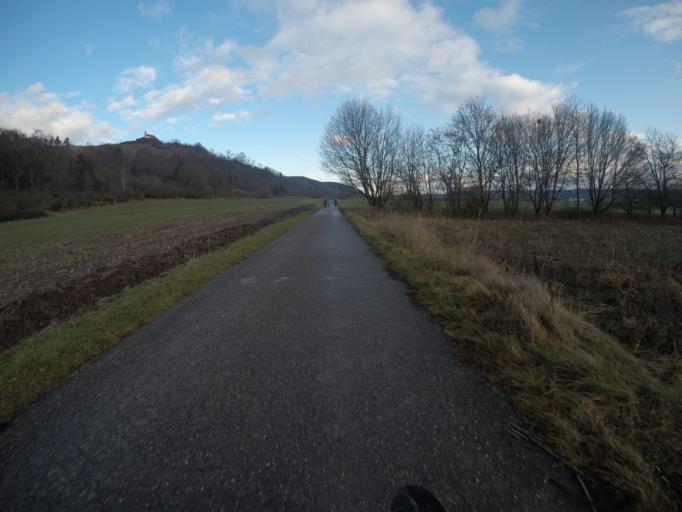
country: DE
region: Baden-Wuerttemberg
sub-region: Tuebingen Region
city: Rottenburg
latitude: 48.5029
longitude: 8.9765
